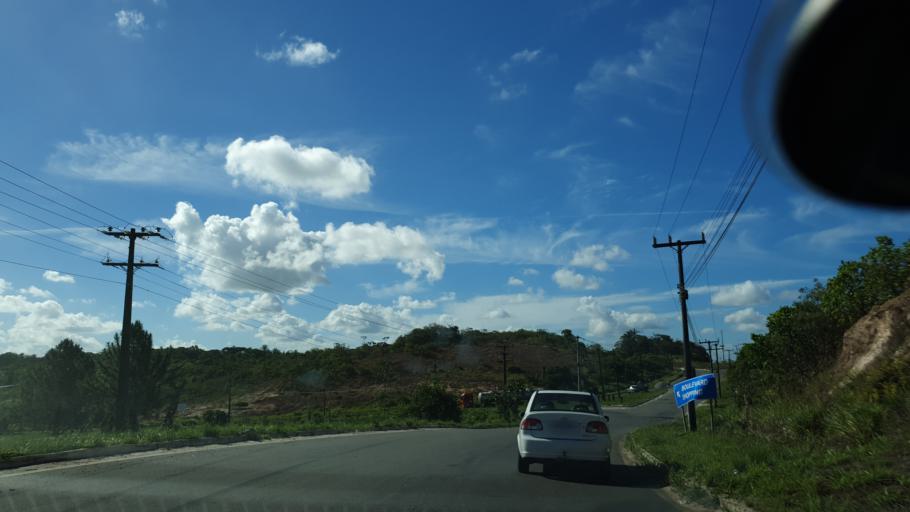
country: BR
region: Bahia
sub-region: Camacari
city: Camacari
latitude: -12.6834
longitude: -38.2801
